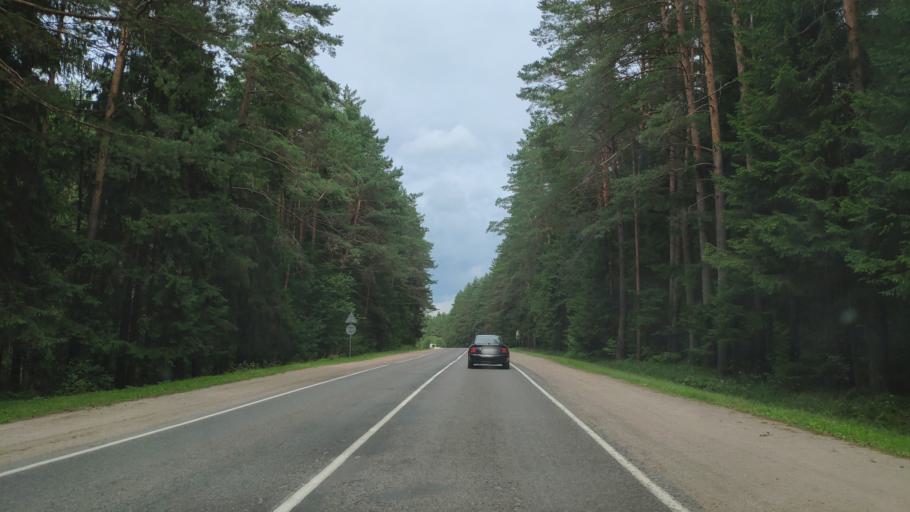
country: BY
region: Minsk
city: Zaslawye
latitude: 53.9787
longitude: 27.2510
